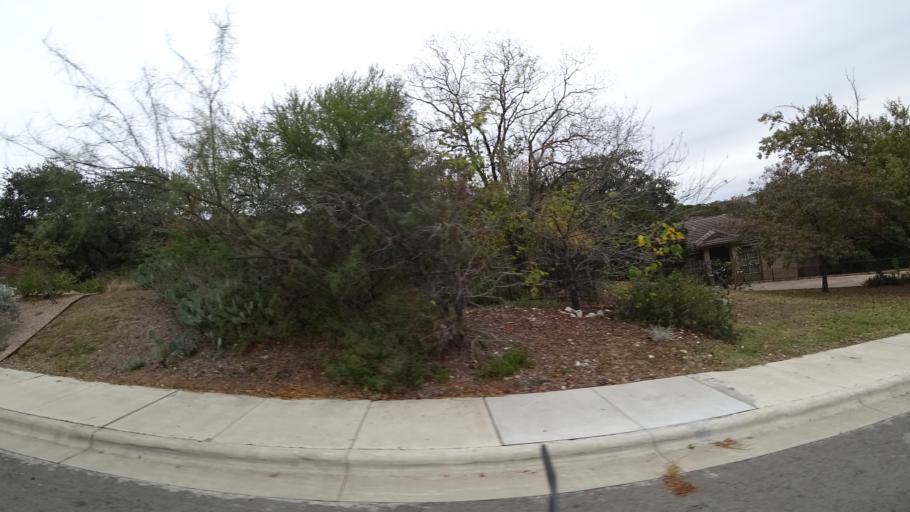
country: US
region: Texas
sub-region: Williamson County
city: Jollyville
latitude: 30.3731
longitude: -97.7991
